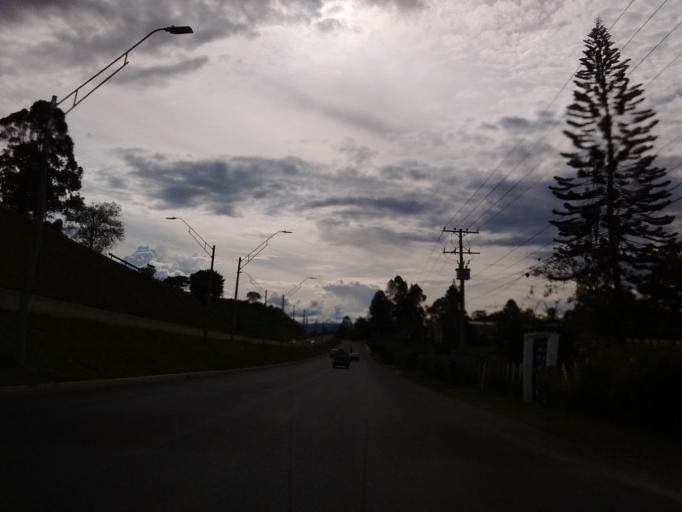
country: CO
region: Antioquia
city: Marinilla
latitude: 6.1672
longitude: -75.3220
